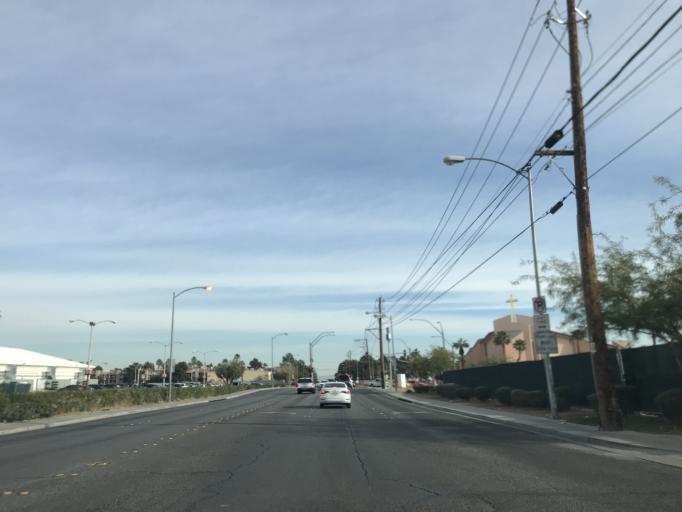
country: US
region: Nevada
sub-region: Clark County
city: Paradise
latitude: 36.0973
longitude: -115.1715
